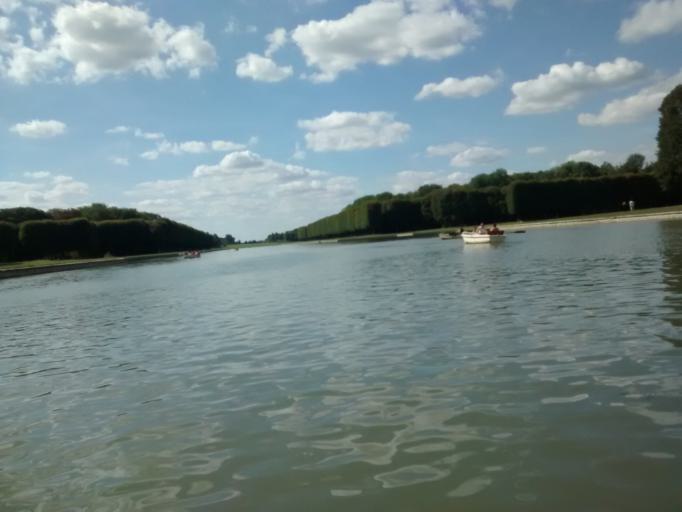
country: FR
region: Ile-de-France
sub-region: Departement des Yvelines
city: Le Chesnay
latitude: 48.8094
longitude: 2.1026
